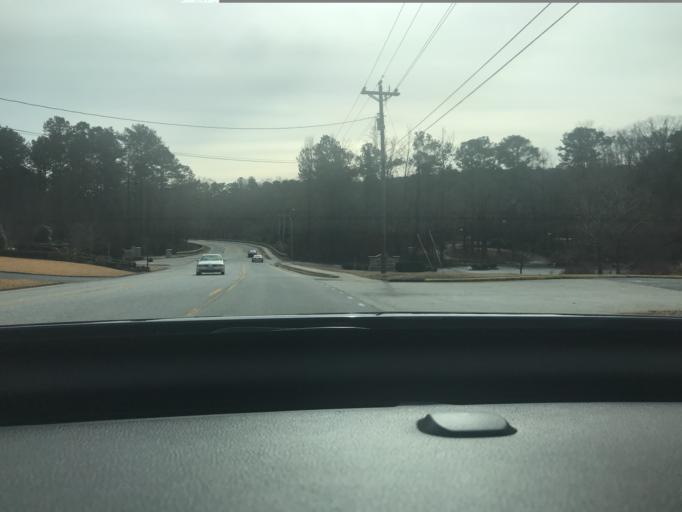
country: US
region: Georgia
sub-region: Gwinnett County
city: Mountain Park
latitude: 33.8763
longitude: -84.0914
